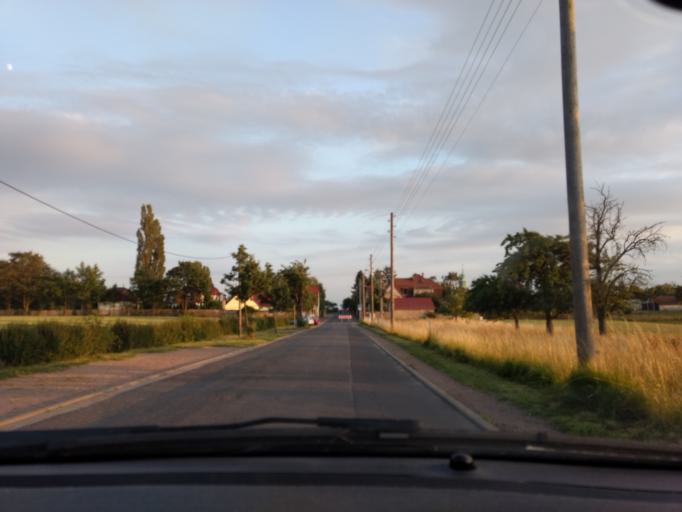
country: DE
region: Saxony
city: Radebeul
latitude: 51.1160
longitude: 13.6686
